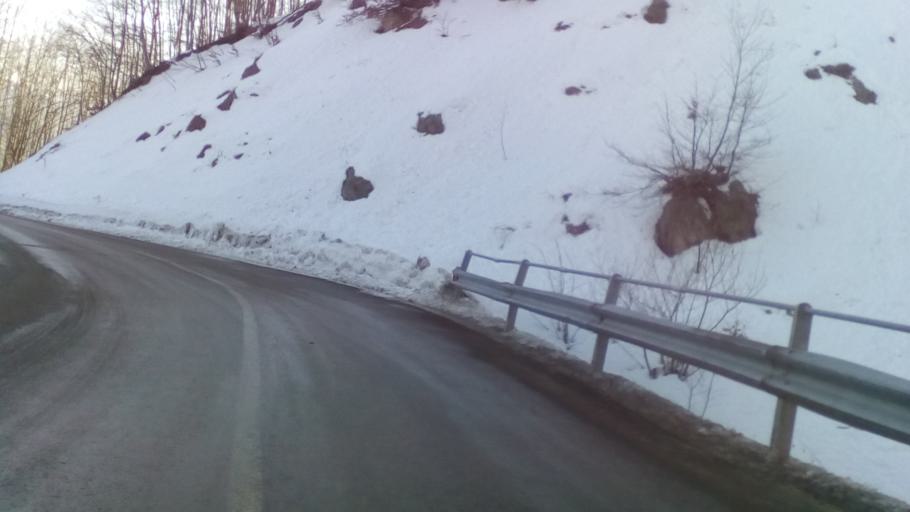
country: IT
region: Tuscany
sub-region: Provincia di Lucca
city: Fosciandora
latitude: 44.2028
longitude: 10.4965
